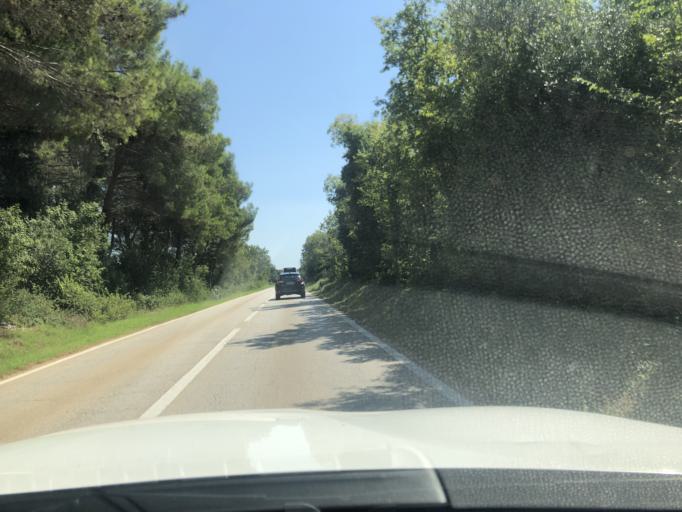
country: HR
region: Istarska
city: Vodnjan
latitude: 45.0305
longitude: 13.7946
